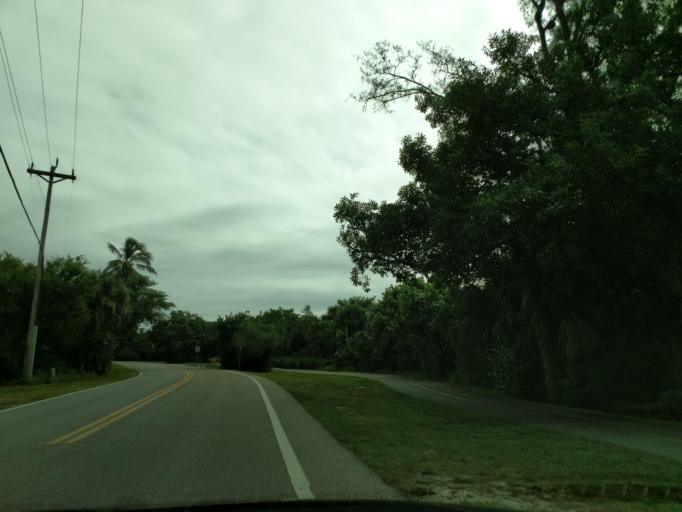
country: US
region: Florida
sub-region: Lee County
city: Sanibel
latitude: 26.4510
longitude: -82.0211
